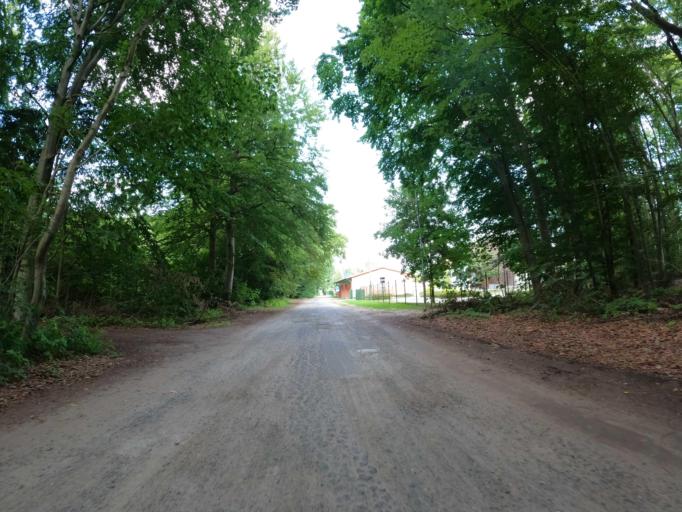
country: DE
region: Mecklenburg-Vorpommern
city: Malchow
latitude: 53.4870
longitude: 12.4340
